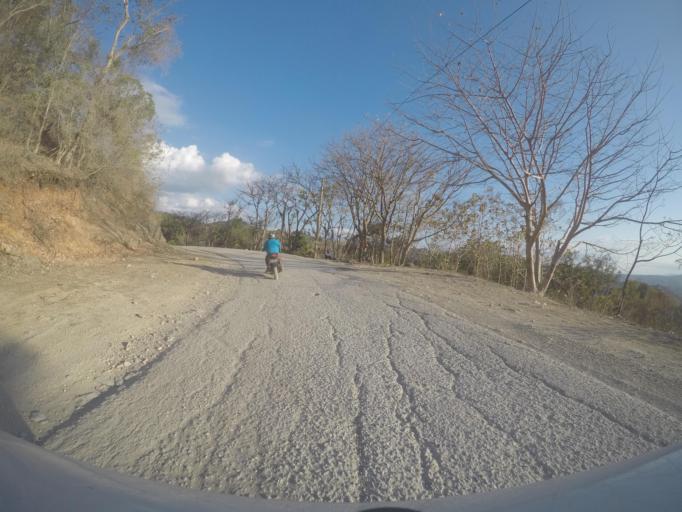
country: TL
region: Bobonaro
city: Maliana
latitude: -8.9641
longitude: 125.0282
